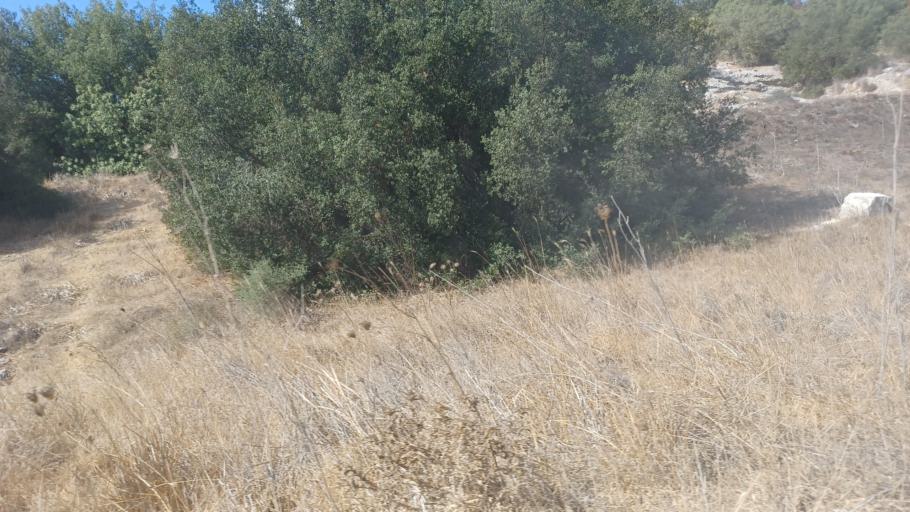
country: CY
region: Pafos
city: Mesogi
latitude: 34.8423
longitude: 32.5482
